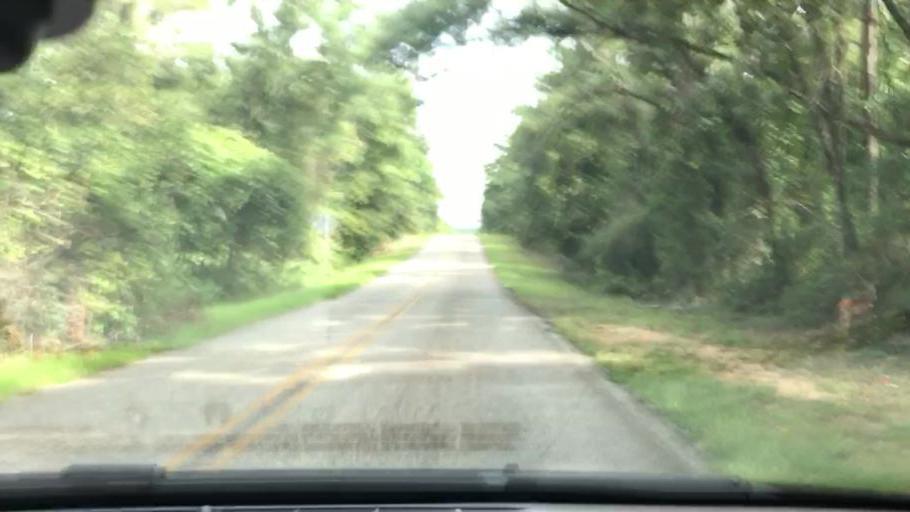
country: US
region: Georgia
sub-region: Early County
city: Blakely
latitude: 31.5080
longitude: -84.9499
